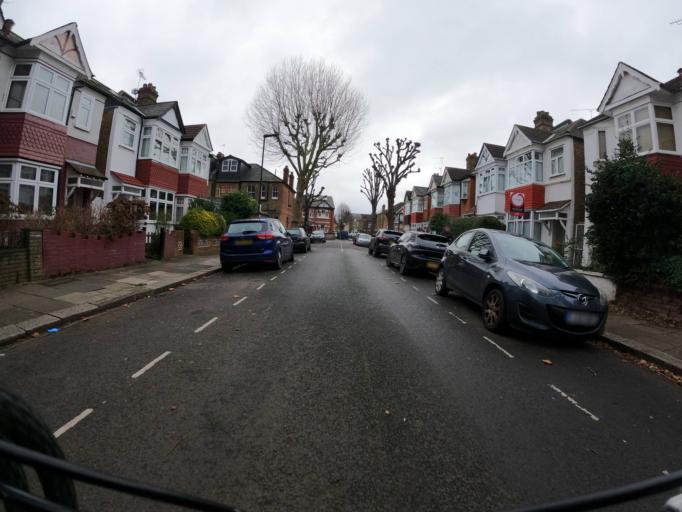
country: GB
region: England
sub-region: Greater London
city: Ealing
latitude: 51.5059
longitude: -0.3225
